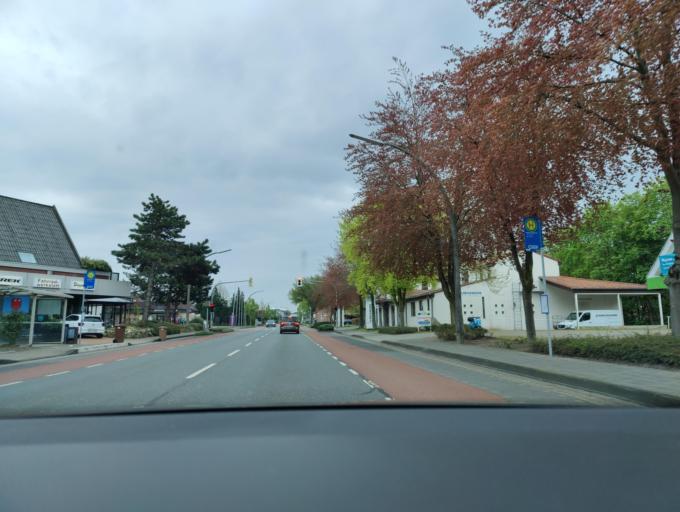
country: DE
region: Lower Saxony
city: Lingen
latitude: 52.5042
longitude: 7.3230
